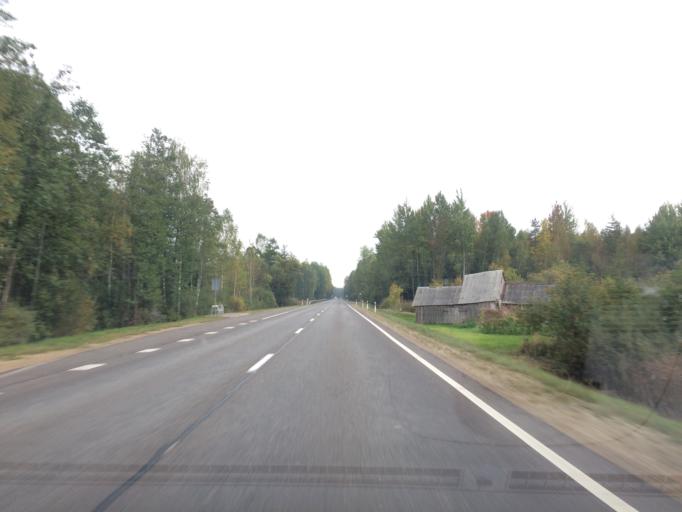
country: LV
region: Livani
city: Livani
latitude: 56.5435
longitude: 26.1225
